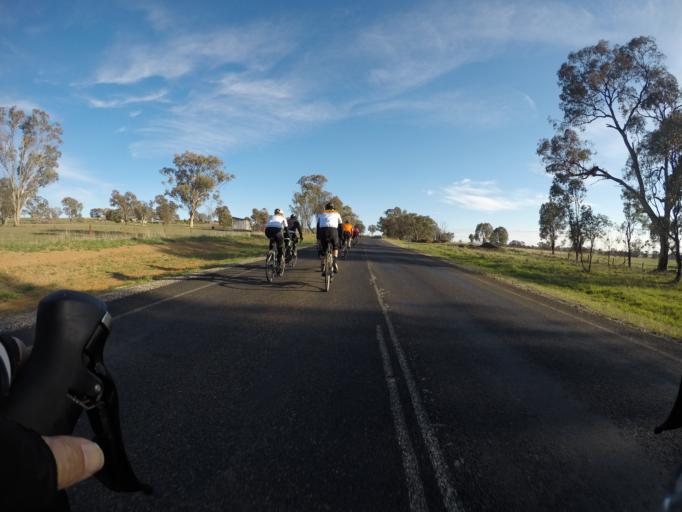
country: AU
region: New South Wales
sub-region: Cabonne
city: Molong
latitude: -32.9726
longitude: 148.7843
